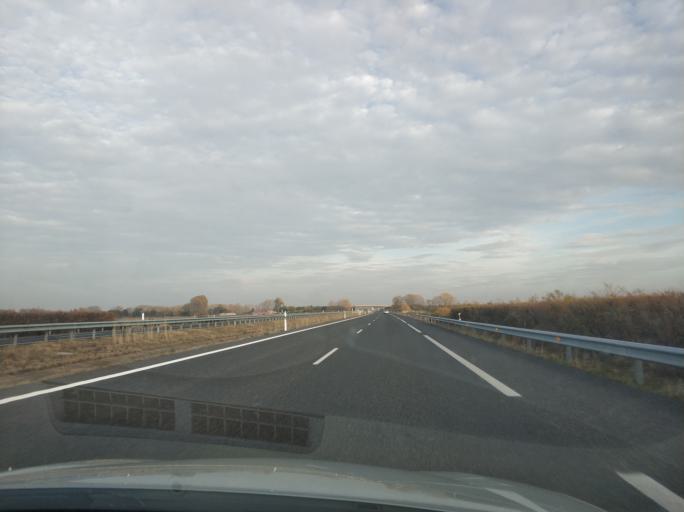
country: ES
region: Castille and Leon
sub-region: Provincia de Palencia
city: Calzada de los Molinos
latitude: 42.3459
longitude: -4.6774
